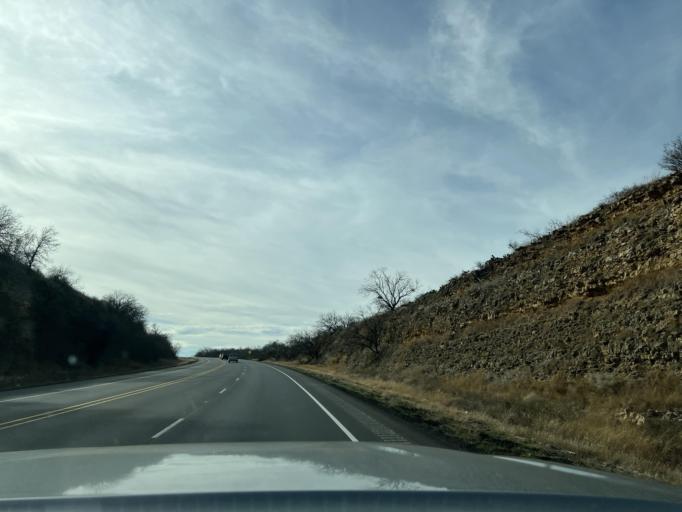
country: US
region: Texas
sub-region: Shackelford County
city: Albany
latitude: 32.7178
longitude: -99.3168
